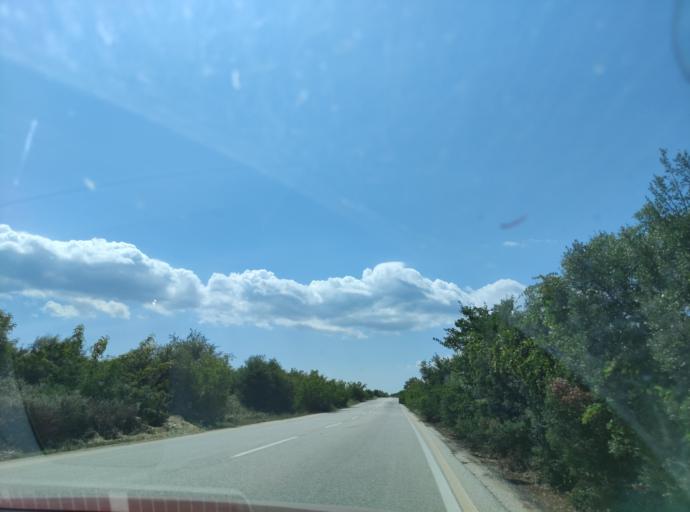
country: GR
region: East Macedonia and Thrace
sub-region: Nomos Kavalas
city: Nikisiani
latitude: 40.9907
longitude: 24.0865
